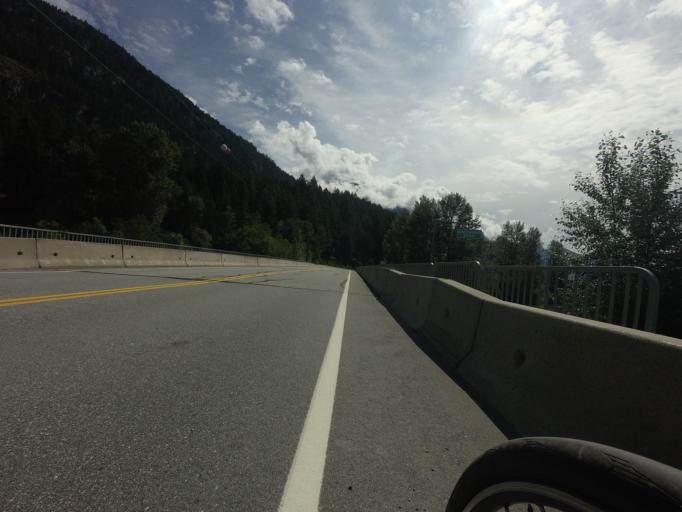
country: CA
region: British Columbia
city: Pemberton
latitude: 50.3073
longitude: -122.6069
